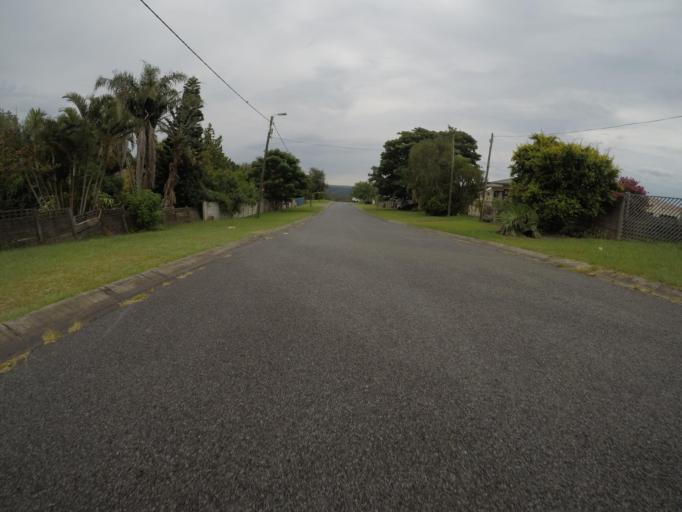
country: ZA
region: Eastern Cape
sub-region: Buffalo City Metropolitan Municipality
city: East London
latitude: -32.9663
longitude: 27.8481
